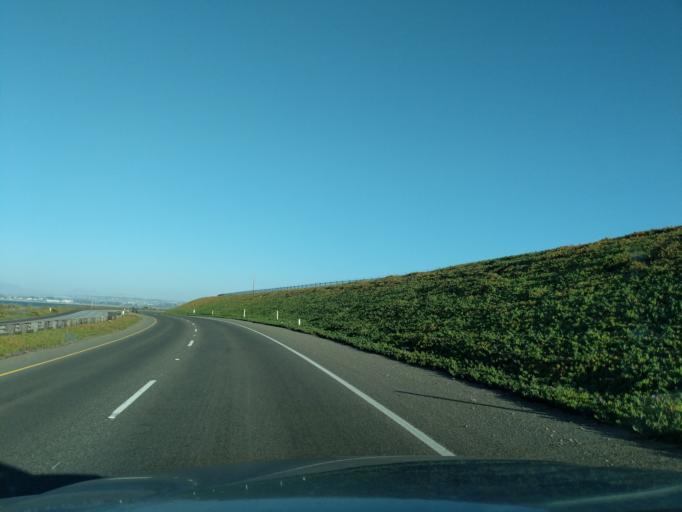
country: US
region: California
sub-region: San Diego County
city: Imperial Beach
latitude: 32.6059
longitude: -117.1294
